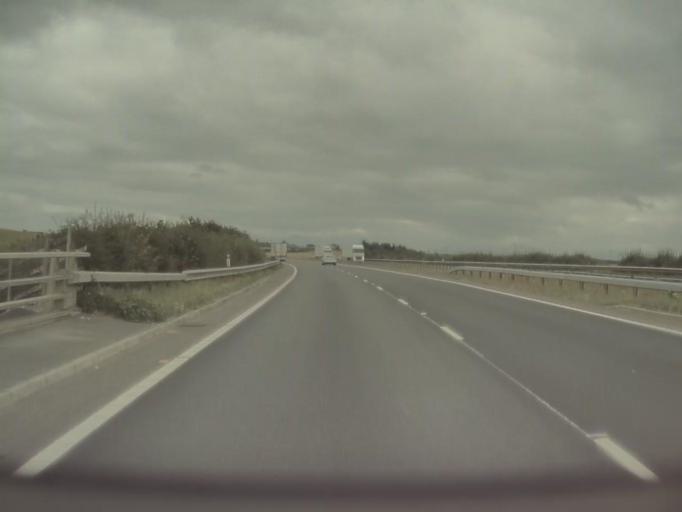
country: GB
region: Wales
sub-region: Anglesey
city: Llanfachraeth
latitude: 53.2657
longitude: -4.4817
